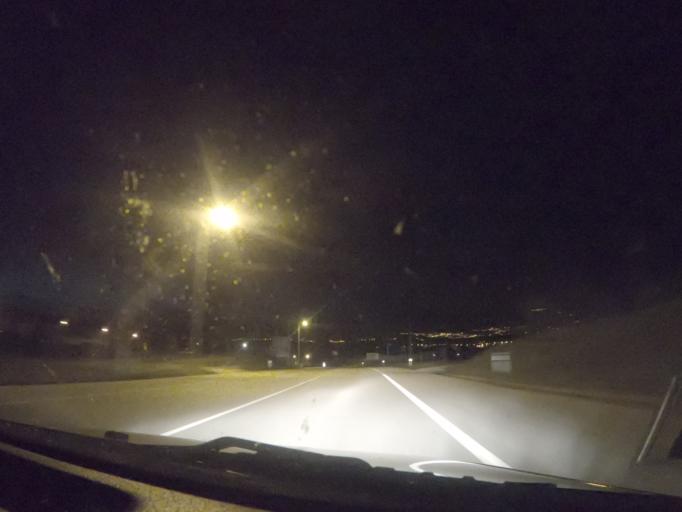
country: PT
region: Castelo Branco
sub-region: Concelho do Fundao
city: Fundao
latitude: 40.1780
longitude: -7.4881
